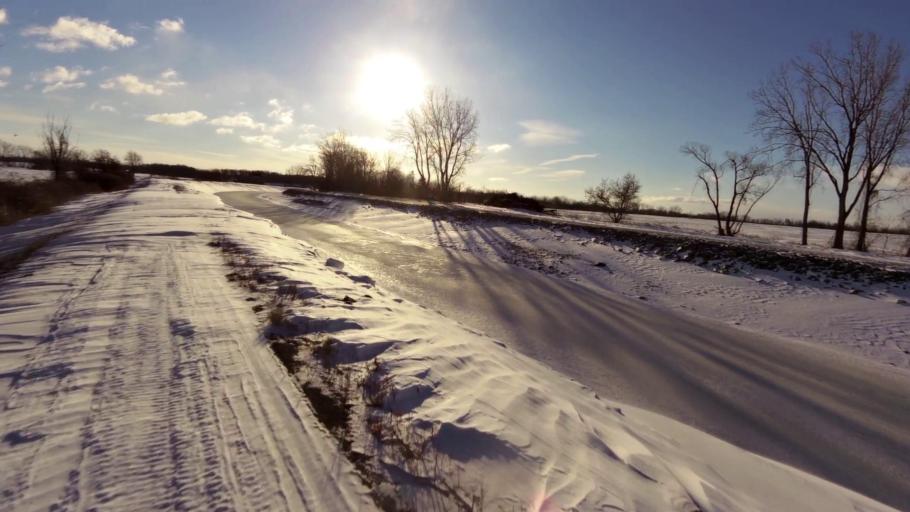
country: US
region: New York
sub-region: Orleans County
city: Albion
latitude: 43.2562
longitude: -78.2289
